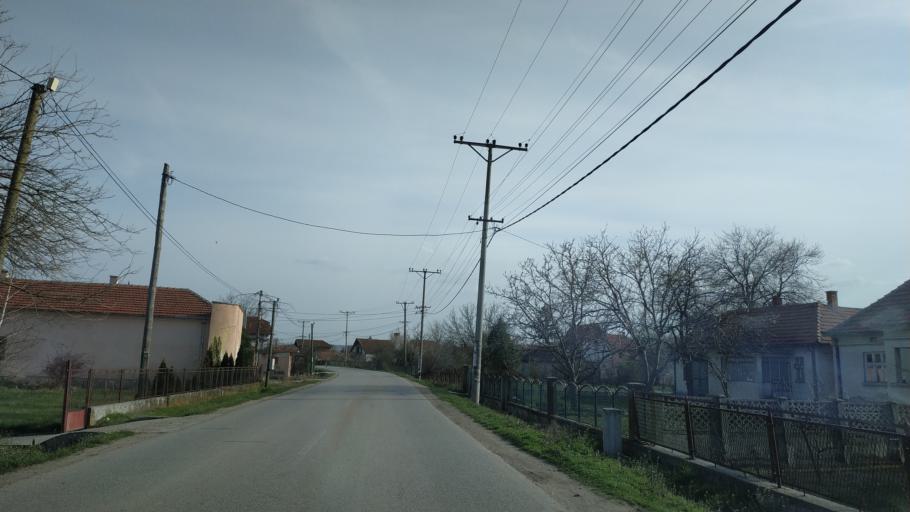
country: RS
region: Central Serbia
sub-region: Nisavski Okrug
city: Aleksinac
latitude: 43.5222
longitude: 21.6647
